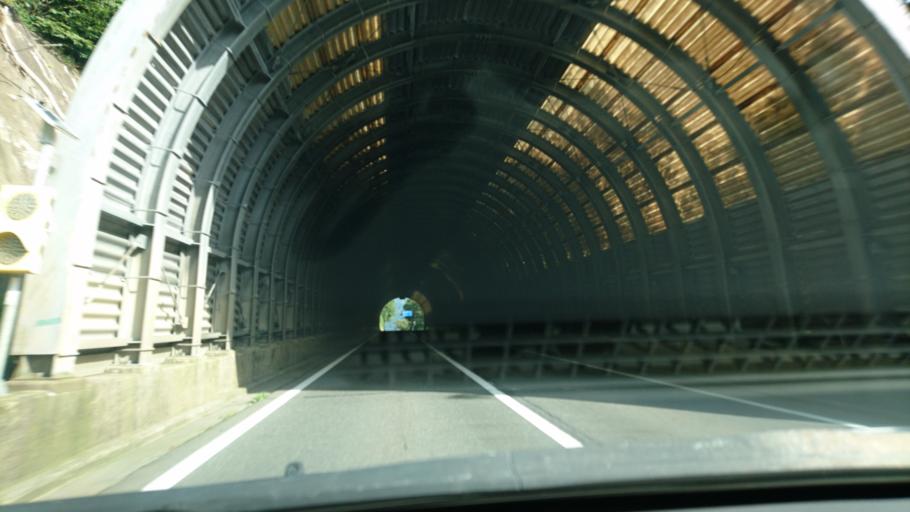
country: JP
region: Iwate
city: Kitakami
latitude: 39.3067
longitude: 140.8537
